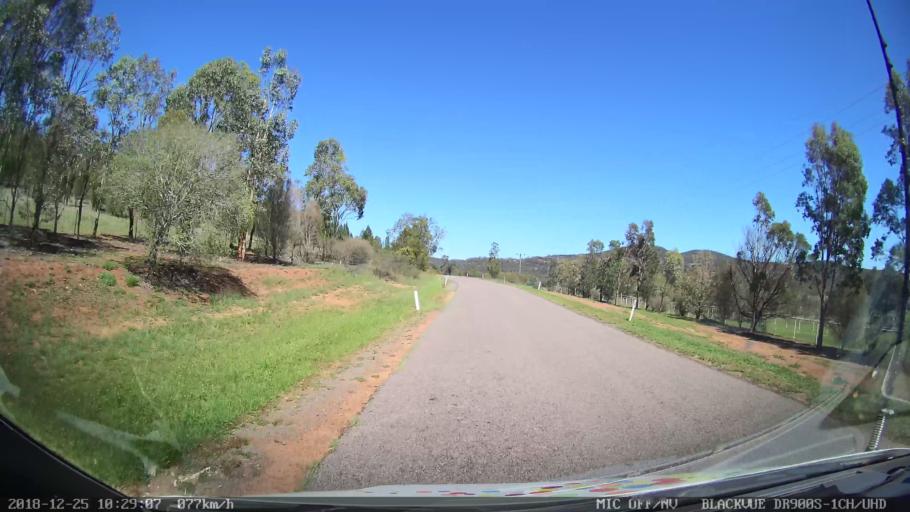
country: AU
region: New South Wales
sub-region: Muswellbrook
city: Denman
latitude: -32.3792
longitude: 150.4557
